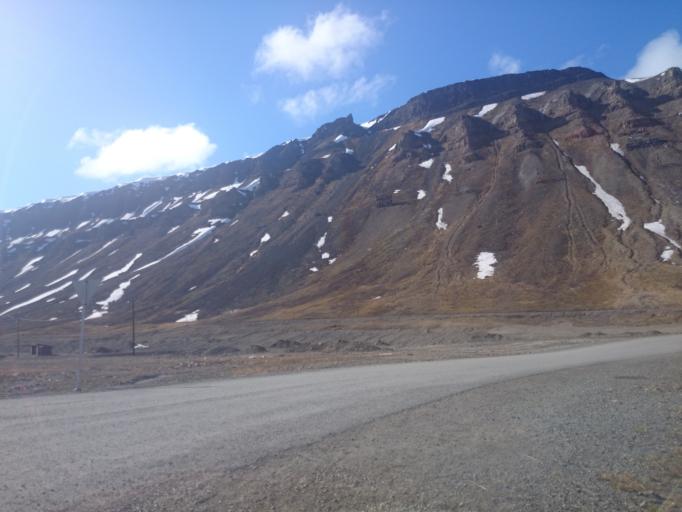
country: SJ
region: Svalbard
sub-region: Spitsbergen
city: Longyearbyen
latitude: 78.2172
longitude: 15.6315
